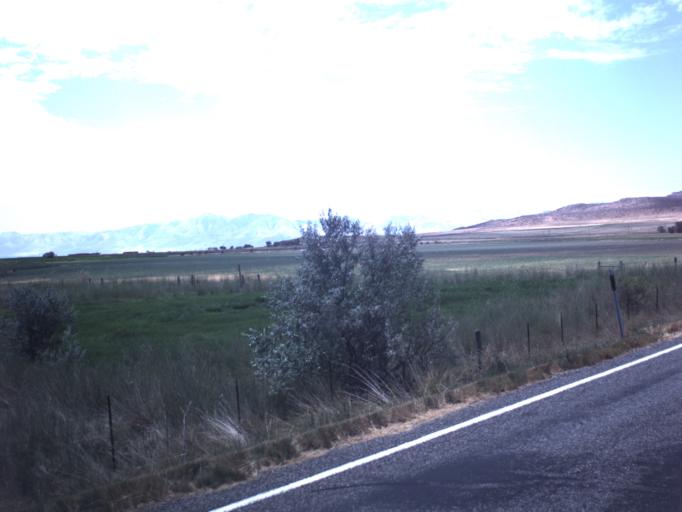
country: US
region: Utah
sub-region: Box Elder County
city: Tremonton
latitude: 41.6369
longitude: -112.3195
